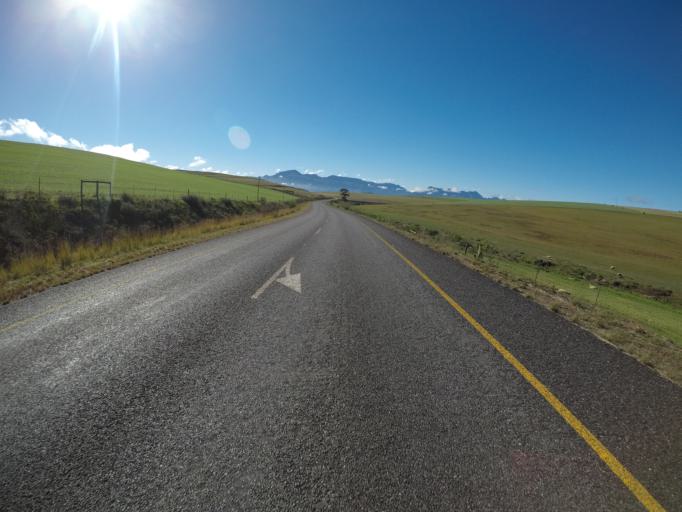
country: ZA
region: Western Cape
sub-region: Overberg District Municipality
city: Caledon
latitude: -34.1373
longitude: 19.5074
